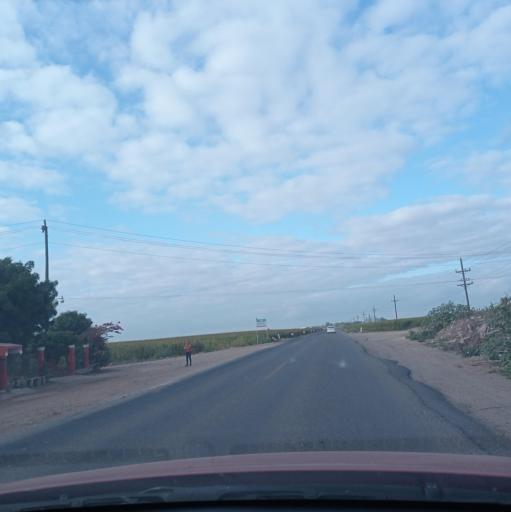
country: MX
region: Sinaloa
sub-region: Guasave
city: Las Quemazones
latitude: 25.6653
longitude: -108.5186
